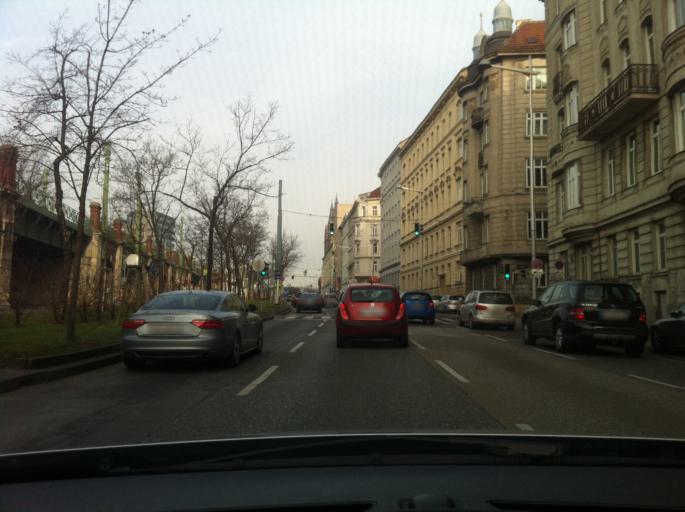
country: AT
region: Vienna
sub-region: Wien Stadt
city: Vienna
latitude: 48.2092
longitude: 16.3391
